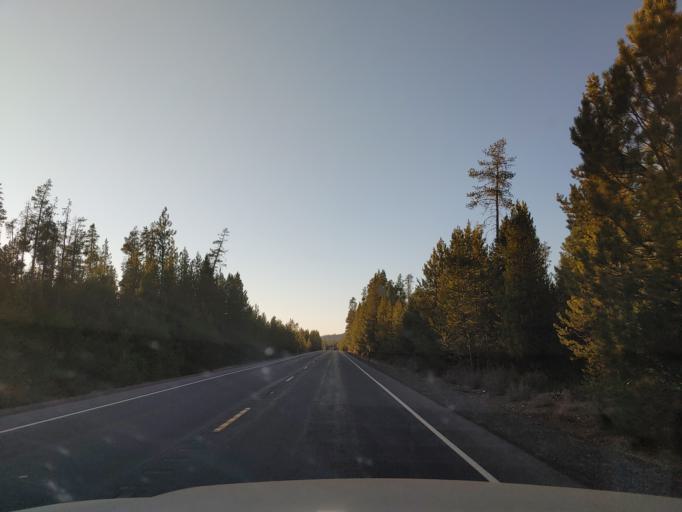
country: US
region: Oregon
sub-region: Deschutes County
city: La Pine
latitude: 43.4123
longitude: -121.8328
